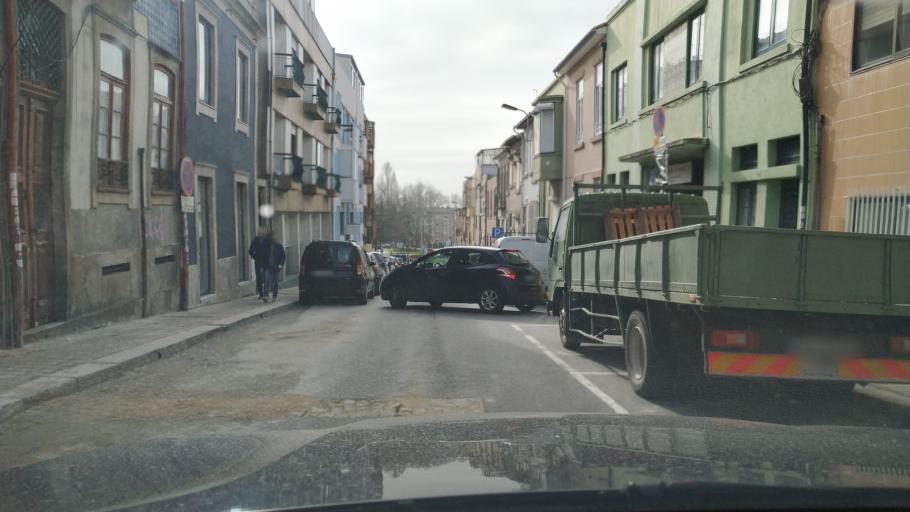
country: PT
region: Porto
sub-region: Matosinhos
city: Senhora da Hora
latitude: 41.1595
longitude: -8.6444
